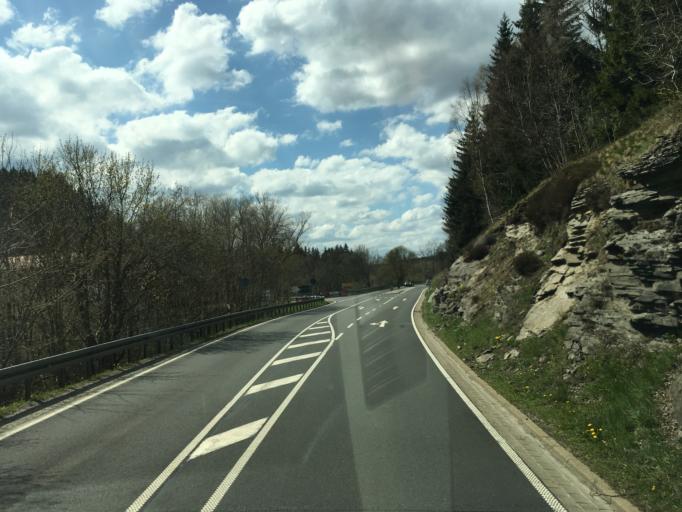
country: DE
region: Saxony-Anhalt
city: Benneckenstein
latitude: 51.6947
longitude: 10.6991
